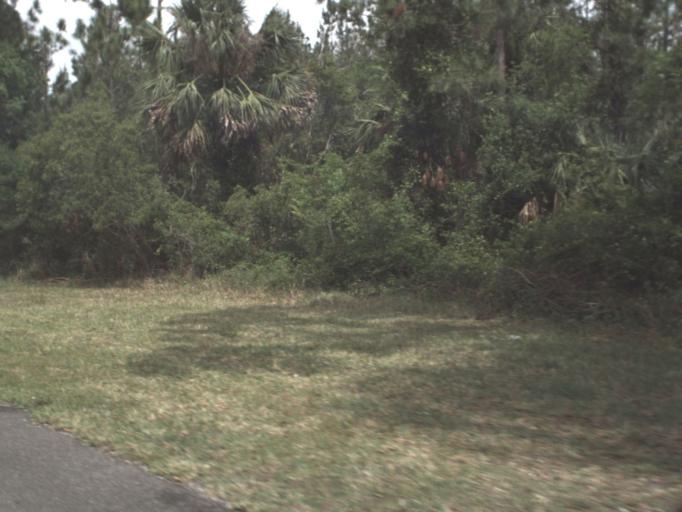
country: US
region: Florida
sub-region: Flagler County
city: Bunnell
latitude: 29.4402
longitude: -81.2810
